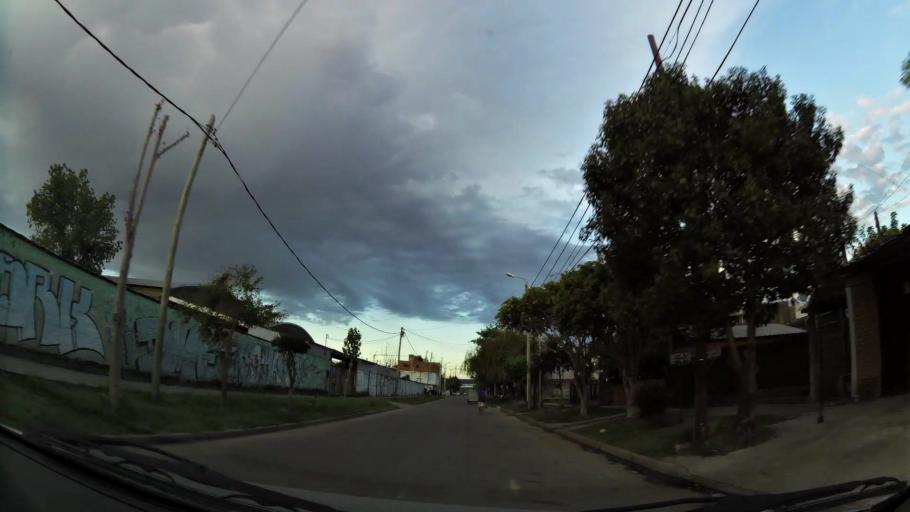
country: AR
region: Buenos Aires
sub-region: Partido de Avellaneda
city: Avellaneda
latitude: -34.6854
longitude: -58.3234
